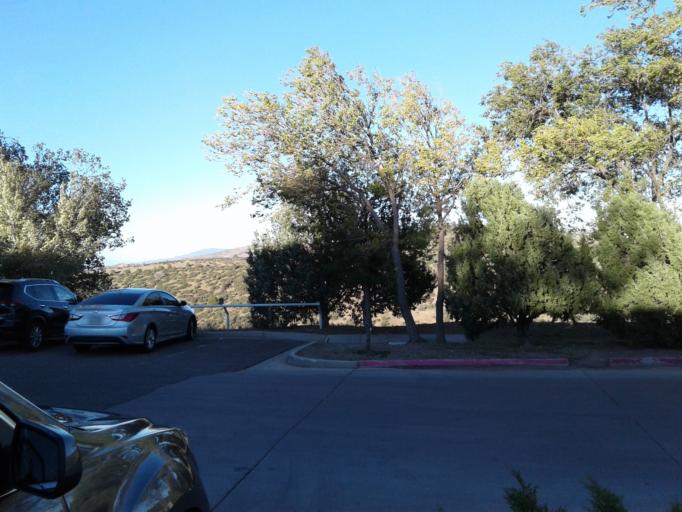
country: US
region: Arizona
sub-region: Yavapai County
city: Prescott
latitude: 34.5503
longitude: -112.4462
